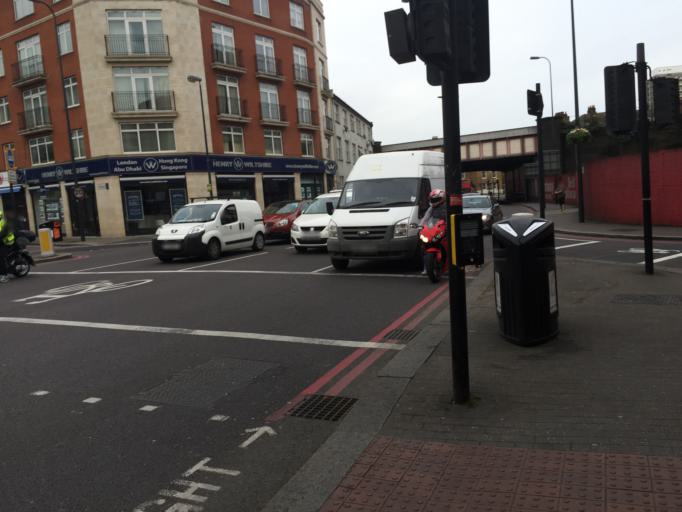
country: GB
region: England
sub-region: Greater London
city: City of Westminster
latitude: 51.4844
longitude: -0.1251
